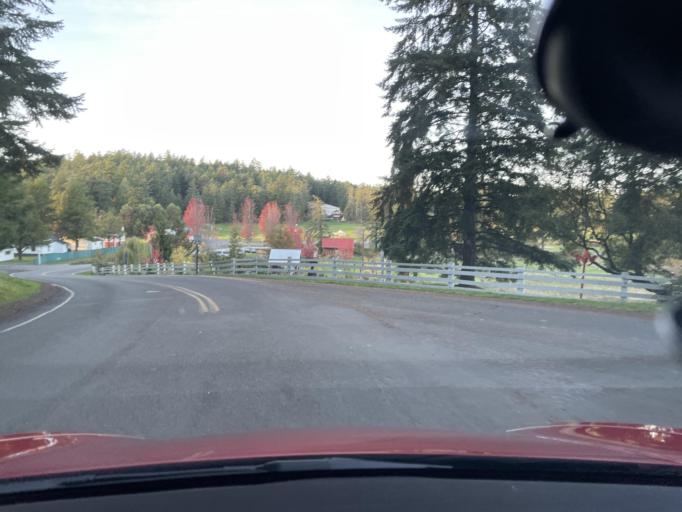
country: US
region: Washington
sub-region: San Juan County
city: Friday Harbor
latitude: 48.6091
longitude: -123.1470
